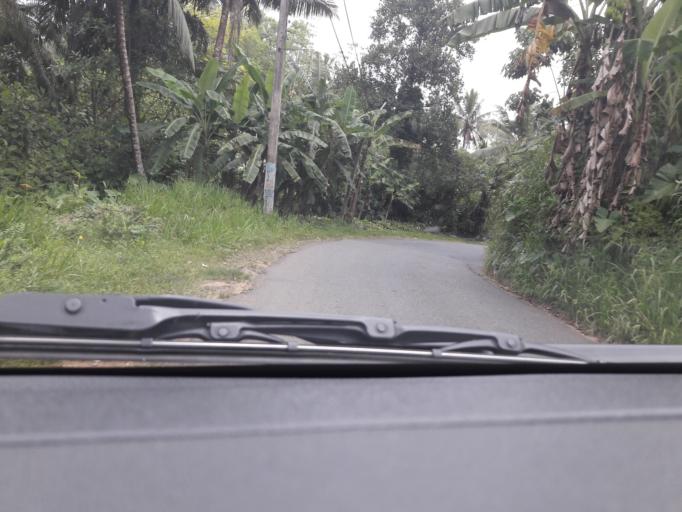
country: LK
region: Southern
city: Hikkaduwa
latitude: 6.2561
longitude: 80.2654
